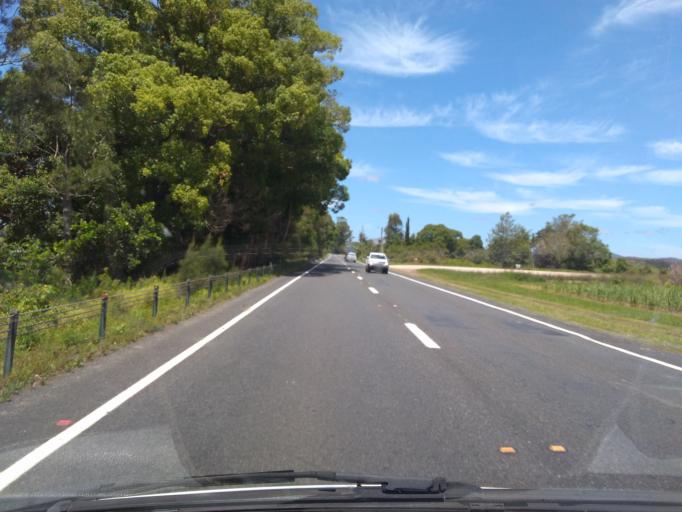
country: AU
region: New South Wales
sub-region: Clarence Valley
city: Maclean
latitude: -29.5418
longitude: 153.1706
